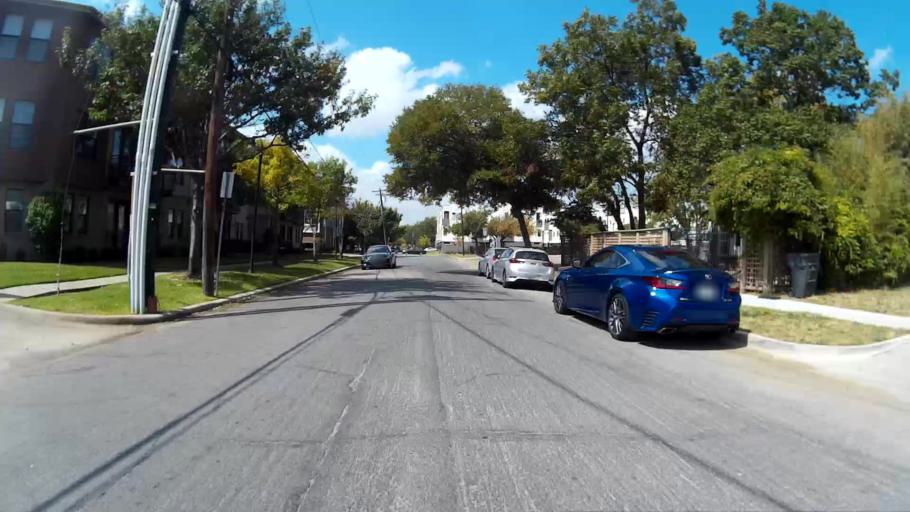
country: US
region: Texas
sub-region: Dallas County
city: Highland Park
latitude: 32.8134
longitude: -96.7712
